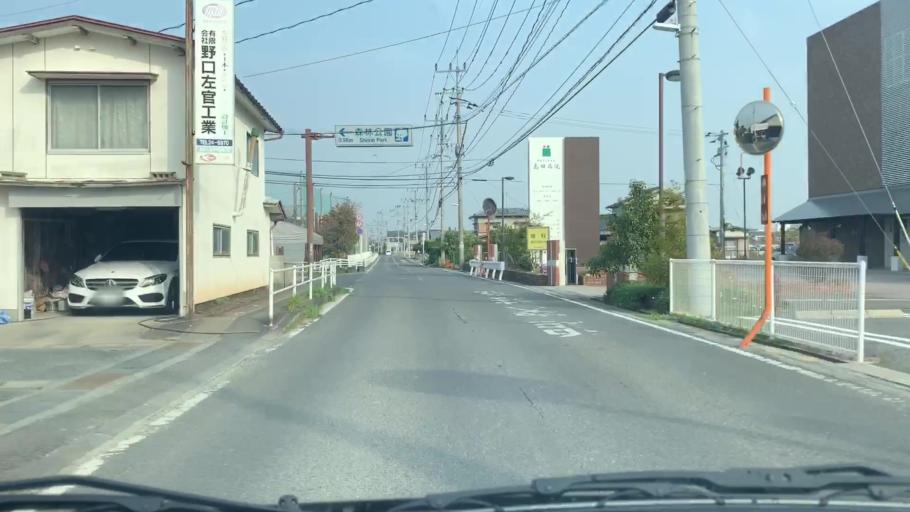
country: JP
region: Saga Prefecture
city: Saga-shi
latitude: 33.2390
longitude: 130.2585
